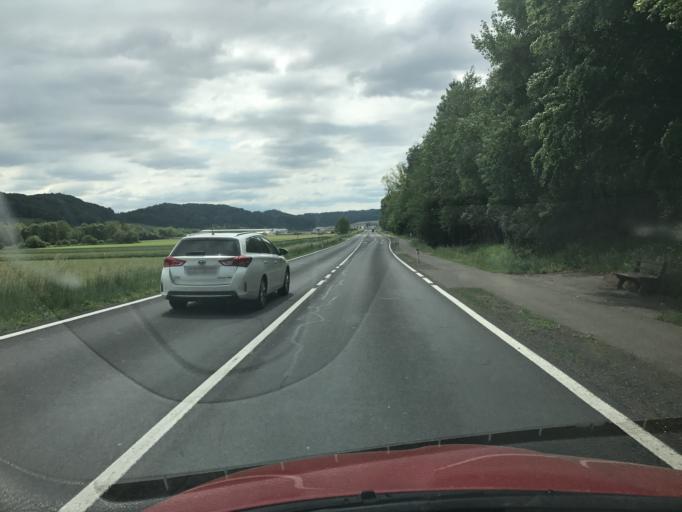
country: AT
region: Styria
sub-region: Politischer Bezirk Suedoststeiermark
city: Kirchbach in Steiermark
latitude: 46.9225
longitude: 15.6692
